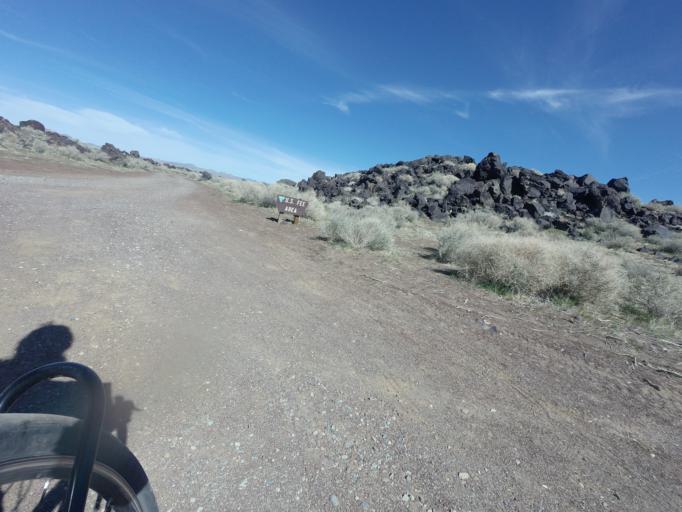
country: US
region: California
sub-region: Kern County
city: Inyokern
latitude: 35.9728
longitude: -117.9119
